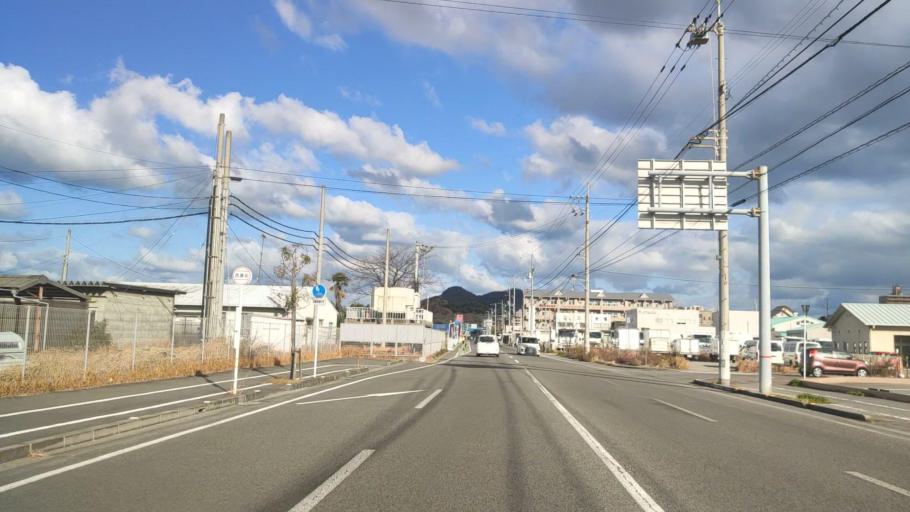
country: JP
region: Ehime
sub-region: Shikoku-chuo Shi
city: Matsuyama
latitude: 33.8580
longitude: 132.7127
